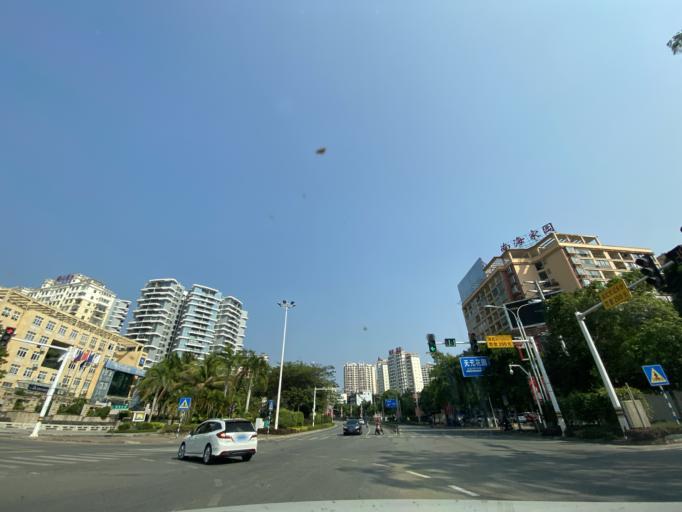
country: CN
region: Hainan
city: Chongshan
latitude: 18.7649
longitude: 109.5227
